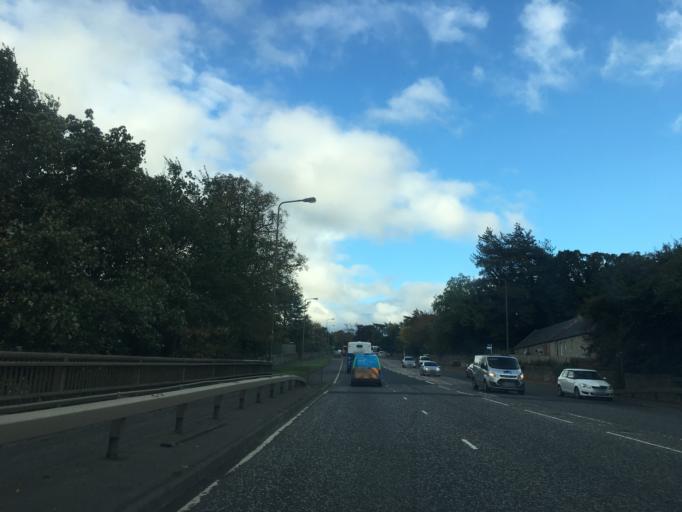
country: GB
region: Scotland
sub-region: Edinburgh
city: Currie
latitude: 55.9641
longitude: -3.3162
